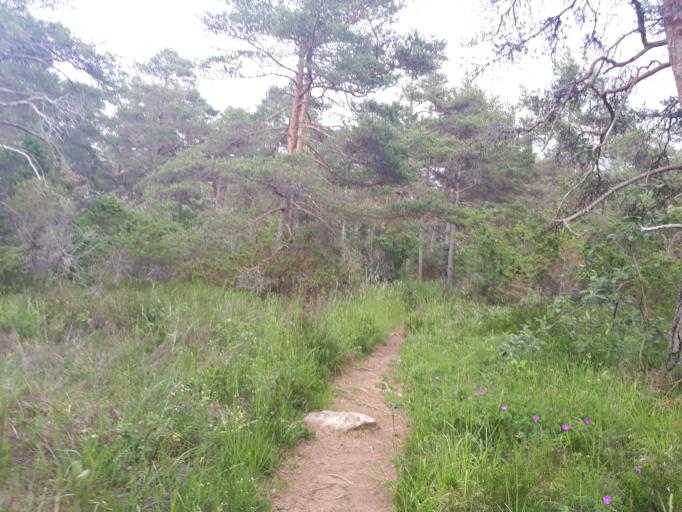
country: SE
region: Gotland
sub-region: Gotland
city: Visby
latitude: 57.6009
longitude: 18.3051
